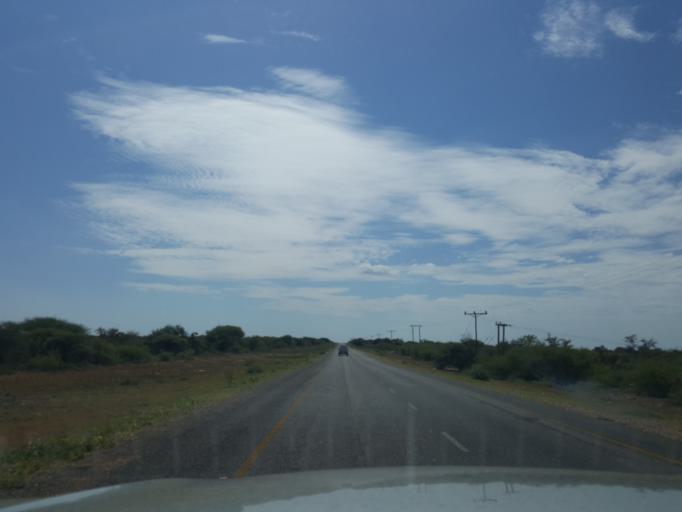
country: BW
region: Kweneng
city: Letlhakeng
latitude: -24.1528
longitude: 25.1584
